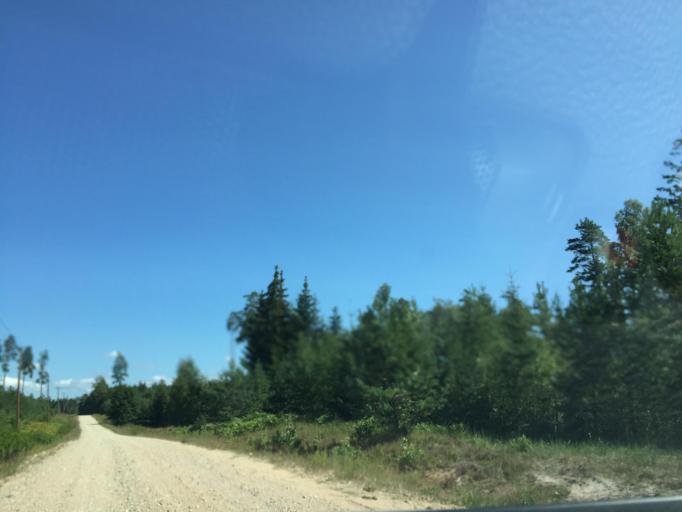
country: LV
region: Talsu Rajons
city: Stende
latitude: 57.1751
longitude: 22.3078
